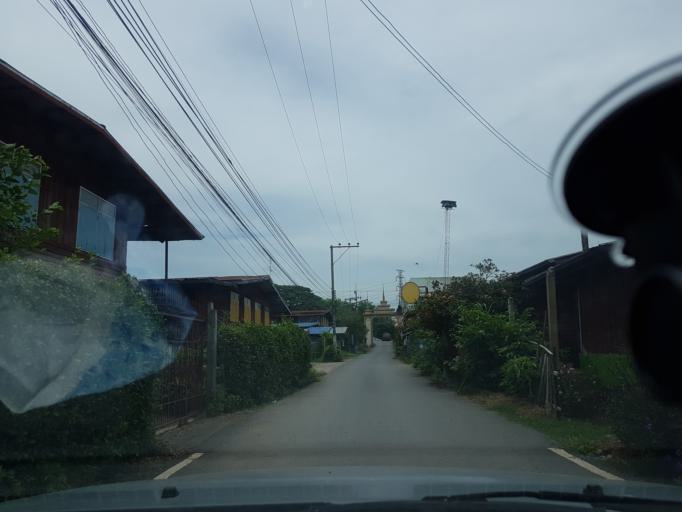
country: TH
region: Lop Buri
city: Tha Wung
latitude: 14.8073
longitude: 100.5763
